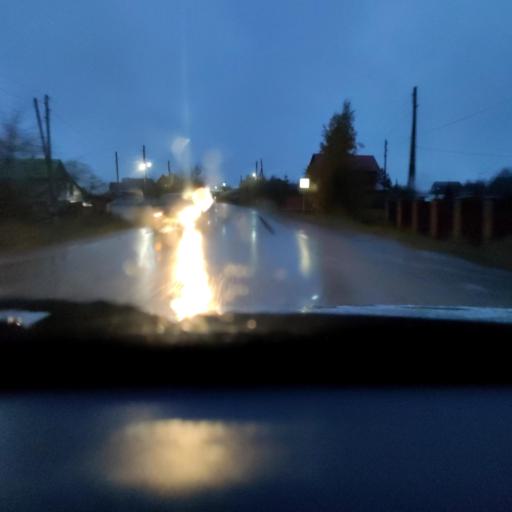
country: RU
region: Perm
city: Kondratovo
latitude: 57.9848
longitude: 56.1027
